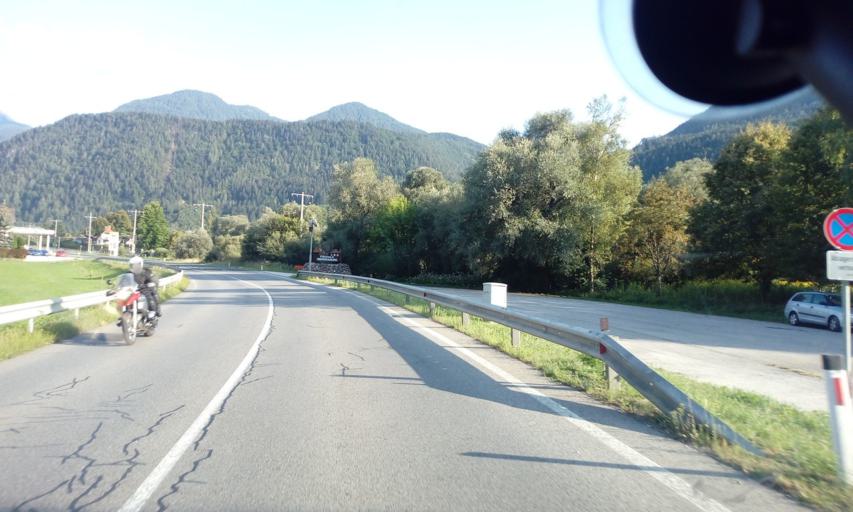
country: AT
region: Carinthia
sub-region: Politischer Bezirk Spittal an der Drau
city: Oberdrauburg
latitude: 46.7506
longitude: 12.9615
